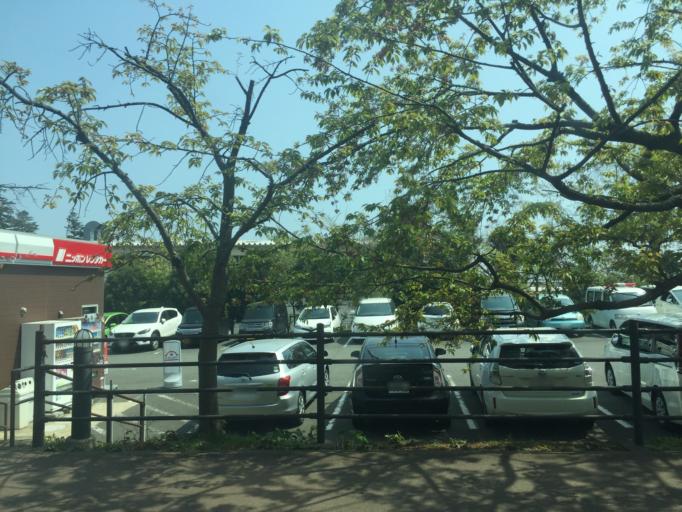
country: JP
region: Shizuoka
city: Ito
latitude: 34.8795
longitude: 139.1091
